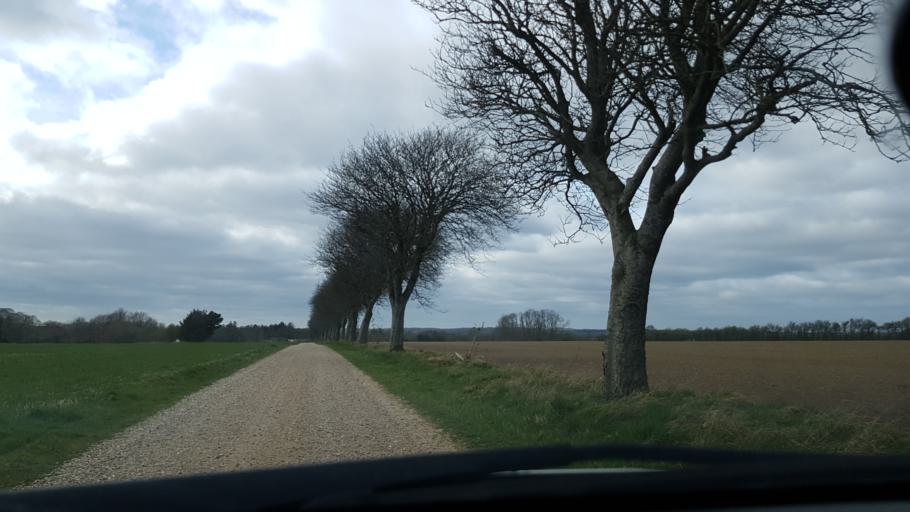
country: DK
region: South Denmark
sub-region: Vejen Kommune
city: Brorup
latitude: 55.4252
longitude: 9.0244
